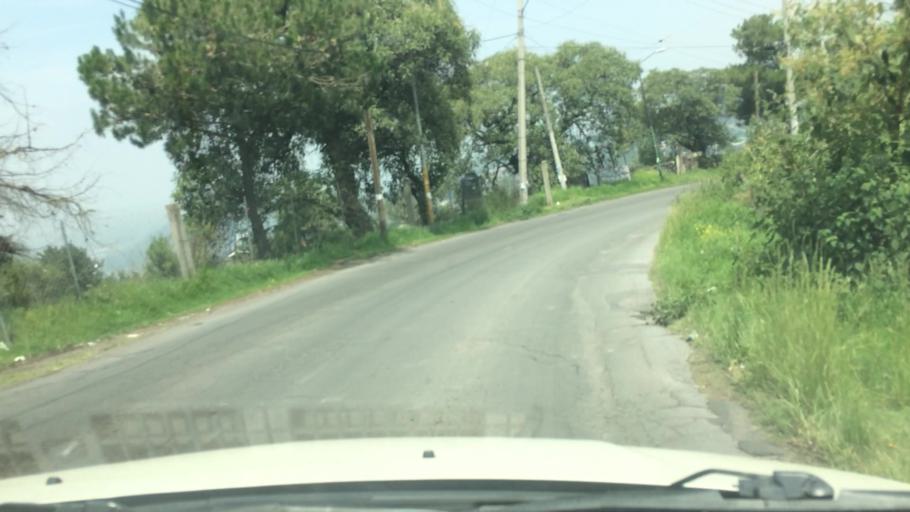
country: MX
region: Mexico City
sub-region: Tlalpan
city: Lomas de Tepemecatl
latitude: 19.2363
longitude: -99.1898
